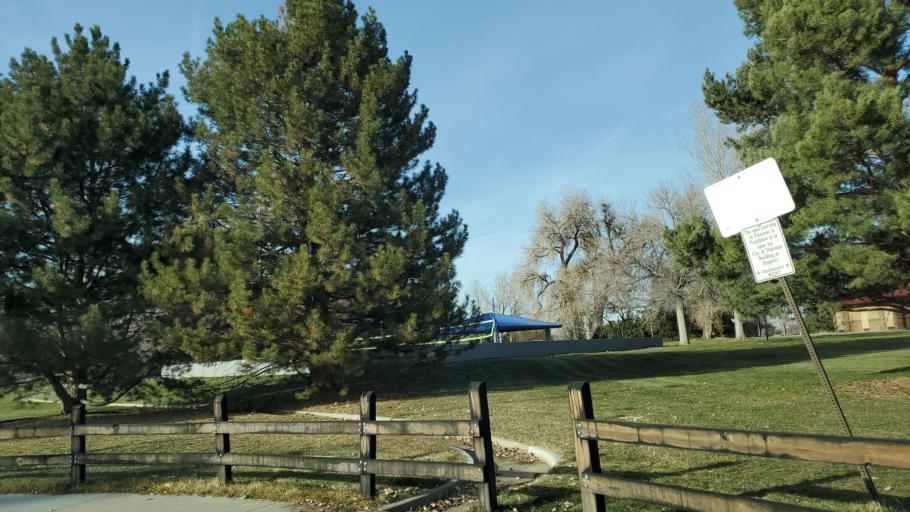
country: US
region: Colorado
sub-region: Adams County
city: Northglenn
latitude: 39.9065
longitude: -104.9500
